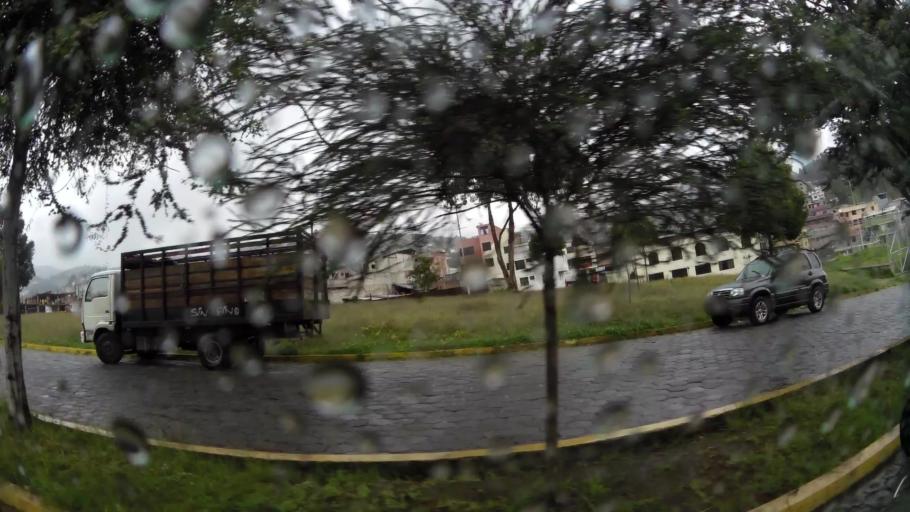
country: EC
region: Pichincha
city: Quito
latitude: -0.0948
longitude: -78.4984
